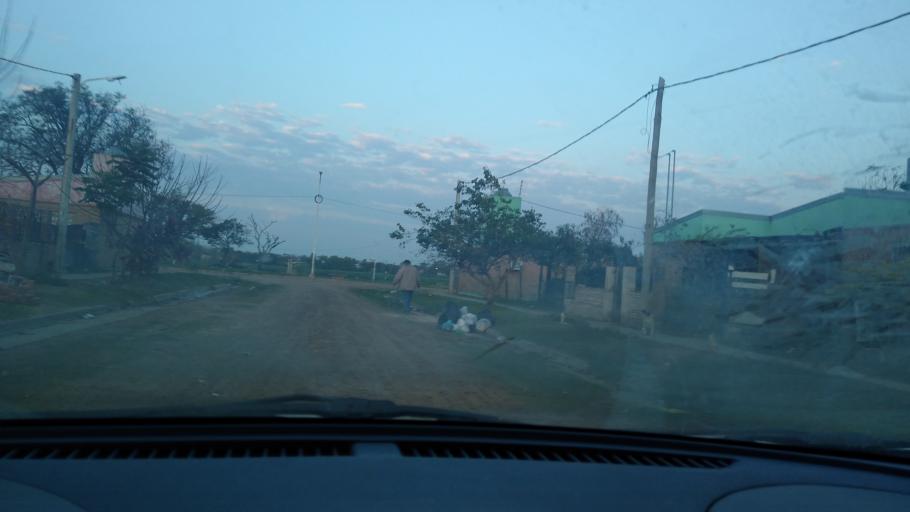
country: AR
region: Chaco
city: Resistencia
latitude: -27.4585
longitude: -58.9647
